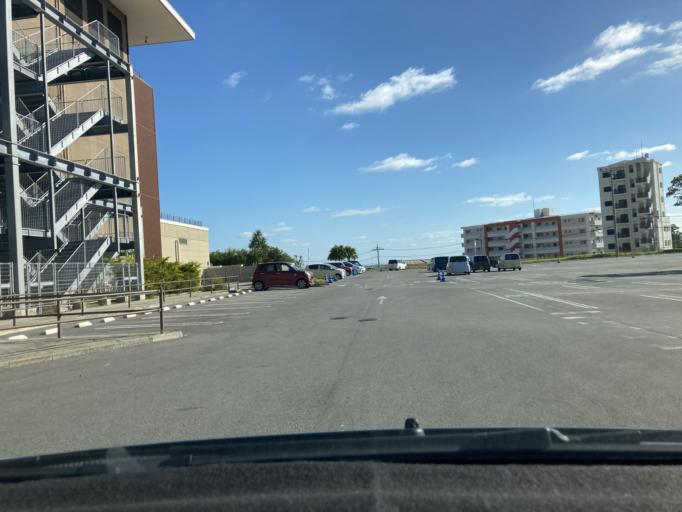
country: JP
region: Okinawa
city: Okinawa
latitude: 26.3137
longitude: 127.7967
